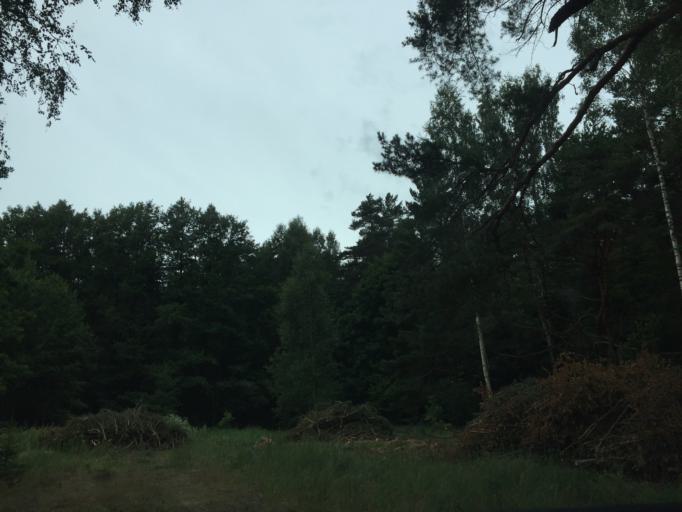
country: LV
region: Saulkrastu
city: Saulkrasti
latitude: 57.4174
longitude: 24.4209
